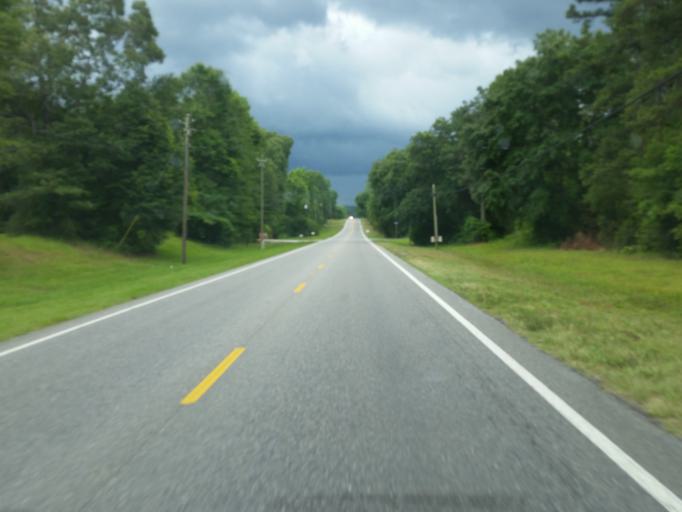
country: US
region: Mississippi
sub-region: Jackson County
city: Hurley
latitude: 30.8135
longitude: -88.3449
